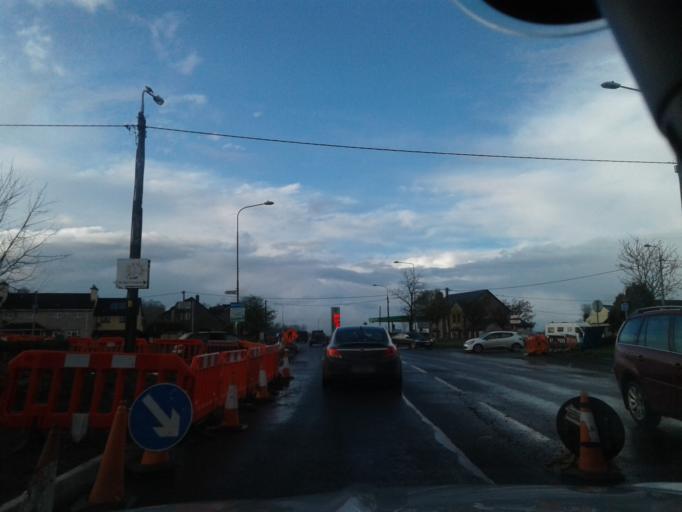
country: IE
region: Ulster
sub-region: County Donegal
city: Leifear
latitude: 54.8349
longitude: -7.4884
